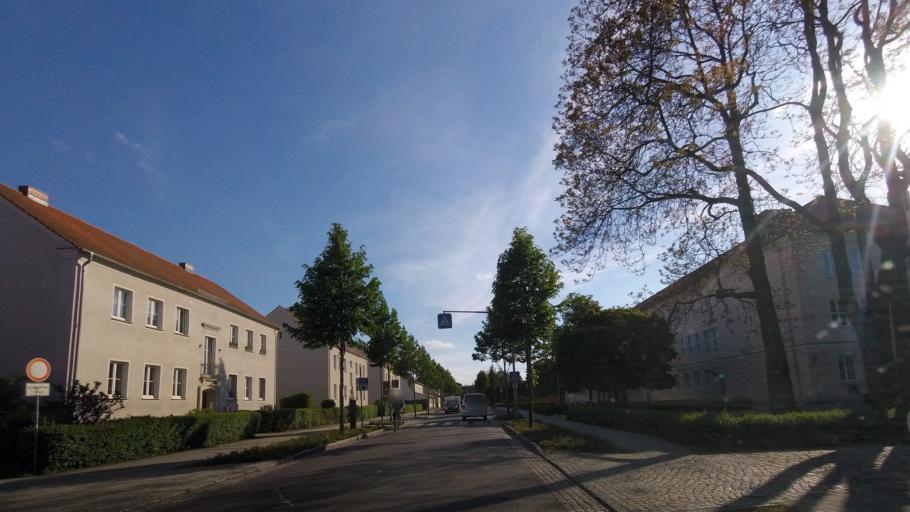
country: DE
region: Brandenburg
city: Lubbenau
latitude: 51.8641
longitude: 13.9632
